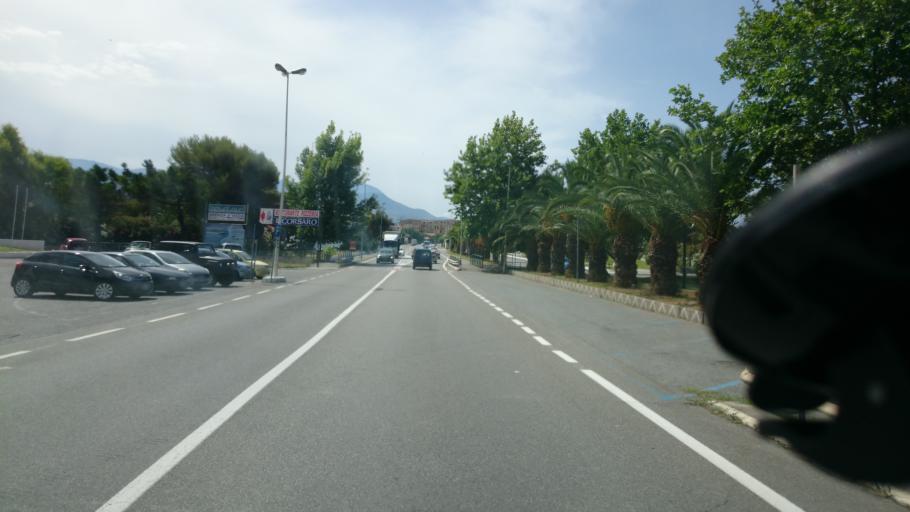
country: IT
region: Calabria
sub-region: Provincia di Cosenza
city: Scalea
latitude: 39.8159
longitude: 15.7877
